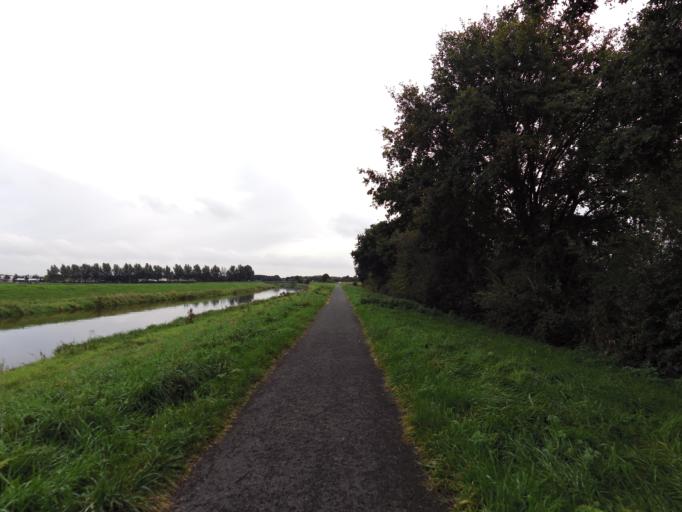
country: DE
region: North Rhine-Westphalia
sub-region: Regierungsbezirk Munster
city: Isselburg
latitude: 51.8572
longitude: 6.4599
